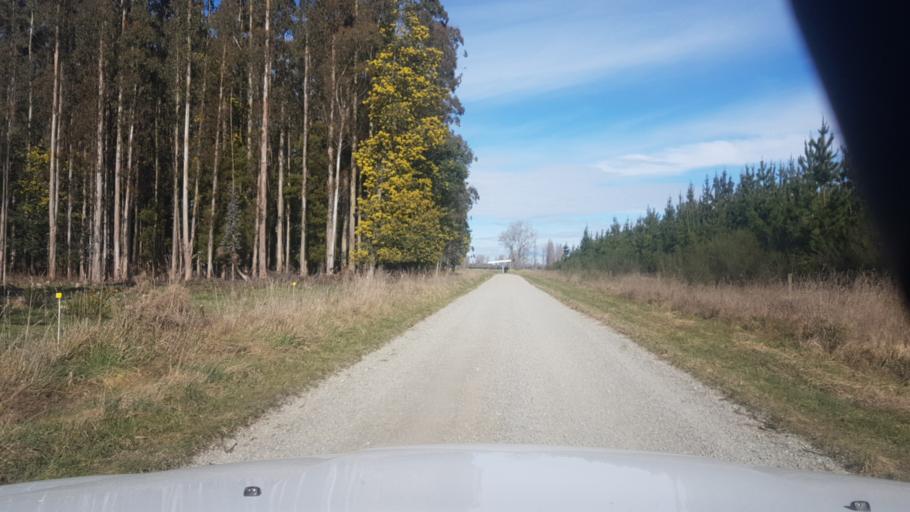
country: NZ
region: Canterbury
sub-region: Timaru District
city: Pleasant Point
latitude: -44.1426
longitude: 171.2747
